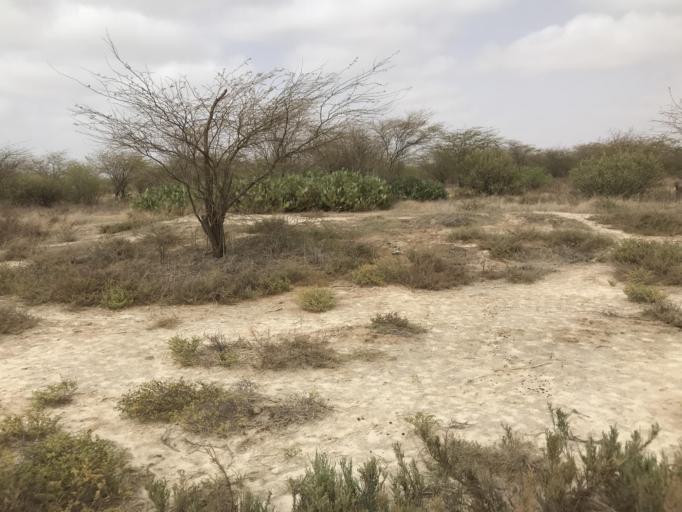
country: SN
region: Saint-Louis
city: Saint-Louis
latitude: 15.9272
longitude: -16.4559
